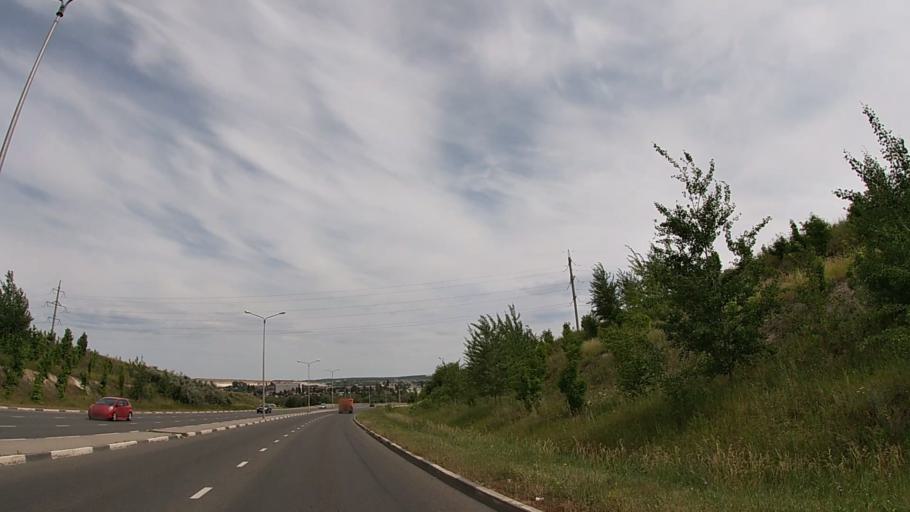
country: RU
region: Belgorod
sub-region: Belgorodskiy Rayon
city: Belgorod
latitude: 50.6042
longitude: 36.5300
